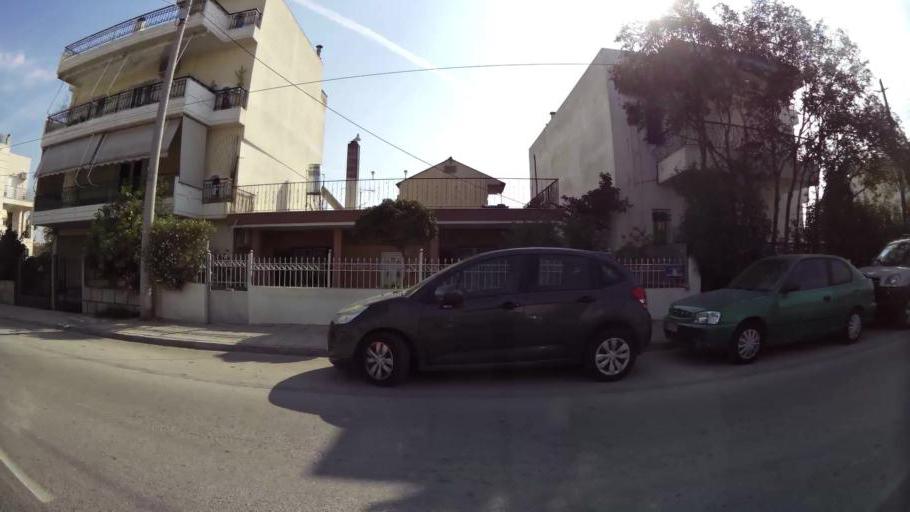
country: GR
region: Attica
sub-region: Nomarchia Athinas
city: Kamateron
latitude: 38.0542
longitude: 23.7097
